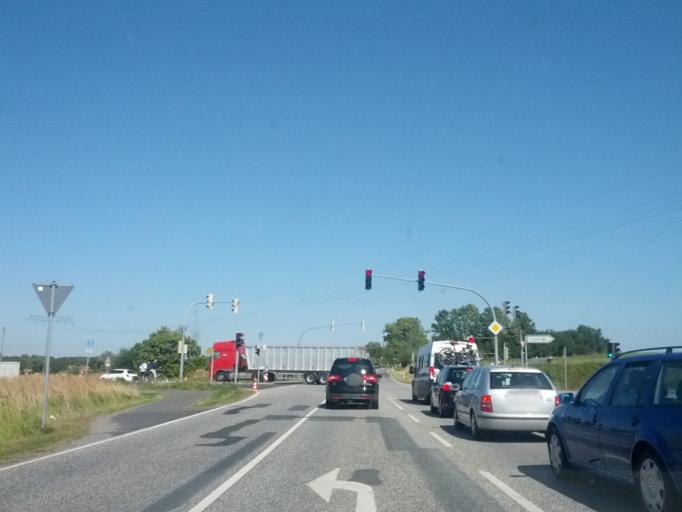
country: DE
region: Mecklenburg-Vorpommern
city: Sagard
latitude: 54.4921
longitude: 13.5790
